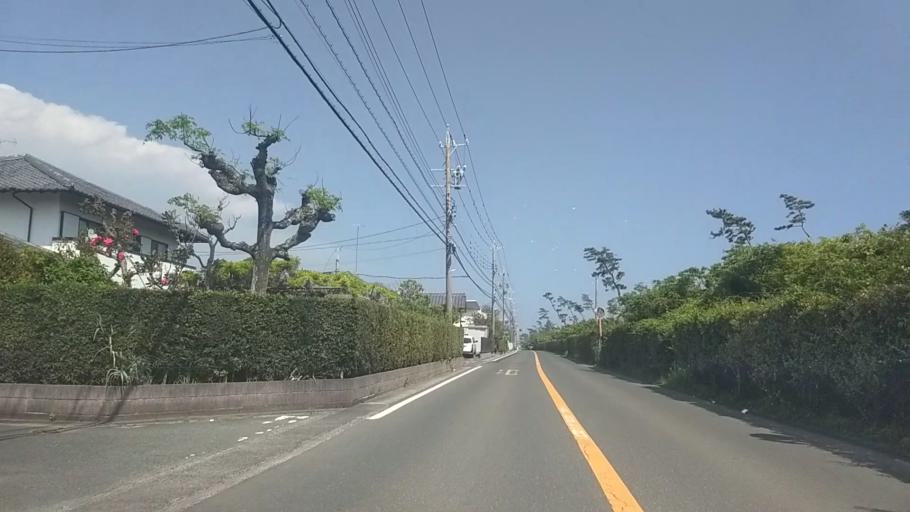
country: JP
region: Shizuoka
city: Hamamatsu
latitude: 34.6671
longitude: 137.7183
